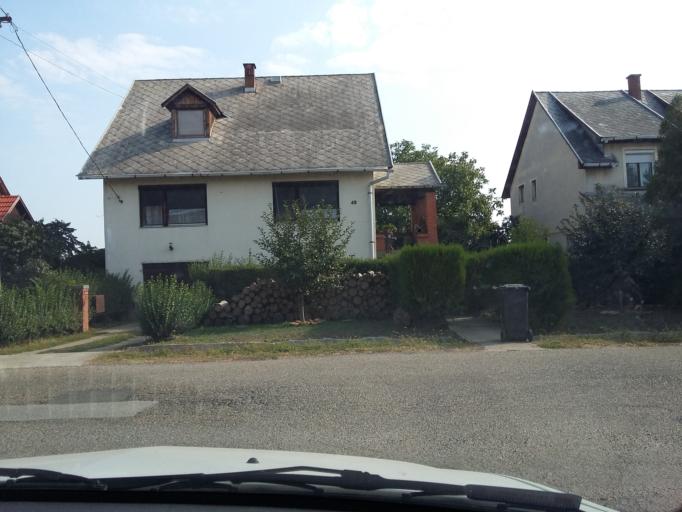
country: HU
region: Borsod-Abauj-Zemplen
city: Bekecs
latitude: 48.1519
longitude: 21.1814
